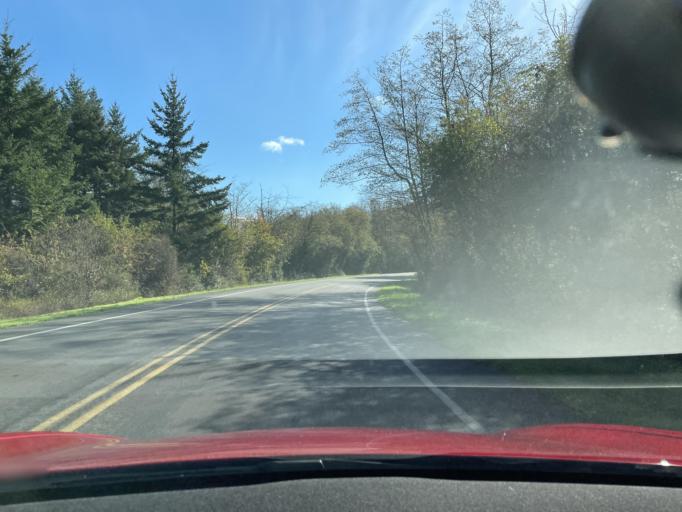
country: US
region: Washington
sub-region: San Juan County
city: Friday Harbor
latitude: 48.4685
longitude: -123.0080
